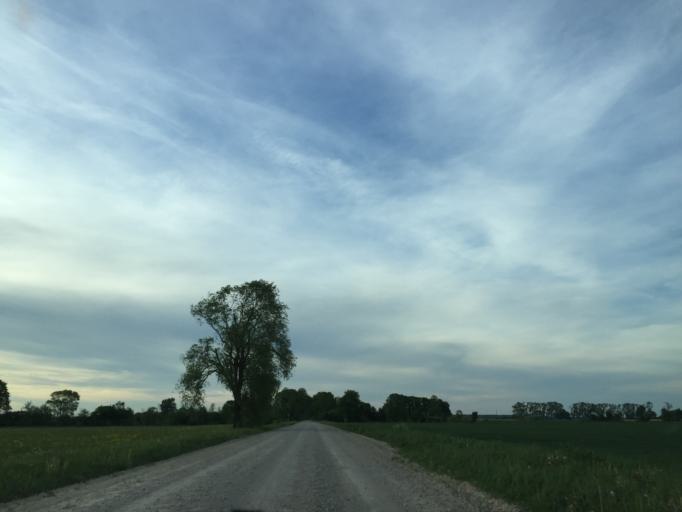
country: LV
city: Tireli
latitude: 56.7023
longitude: 23.4988
